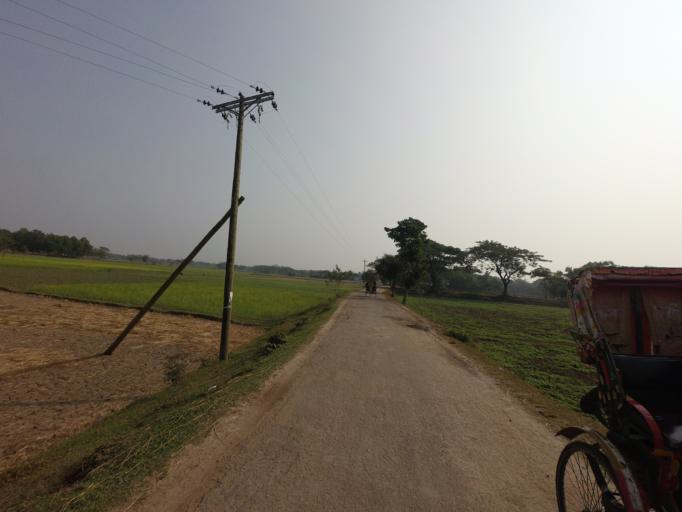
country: BD
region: Dhaka
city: Netrakona
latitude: 25.0097
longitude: 90.6779
